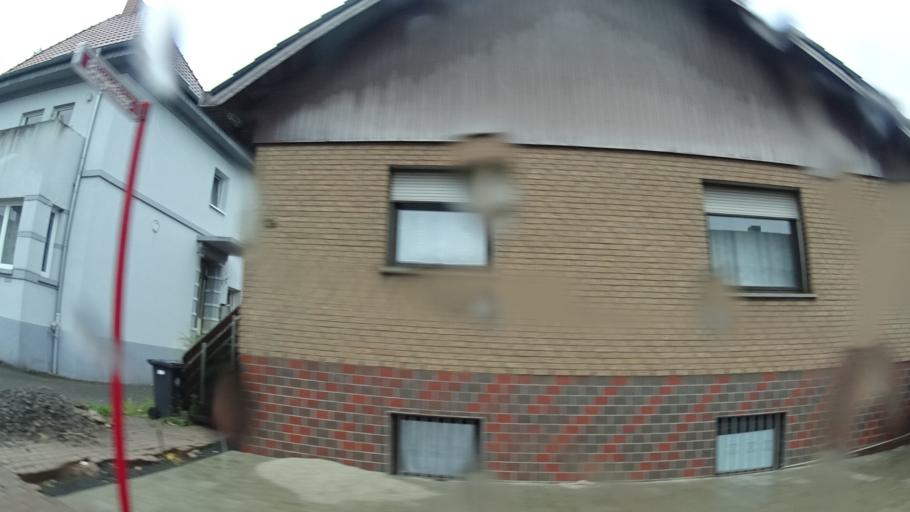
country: DE
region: Rheinland-Pfalz
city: Waldmohr
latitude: 49.3846
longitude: 7.3316
